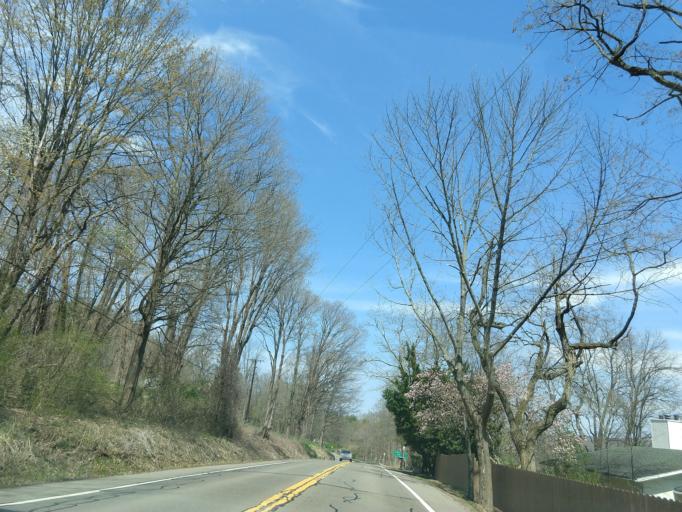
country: US
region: New York
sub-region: Tompkins County
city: Trumansburg
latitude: 42.5425
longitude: -76.5955
